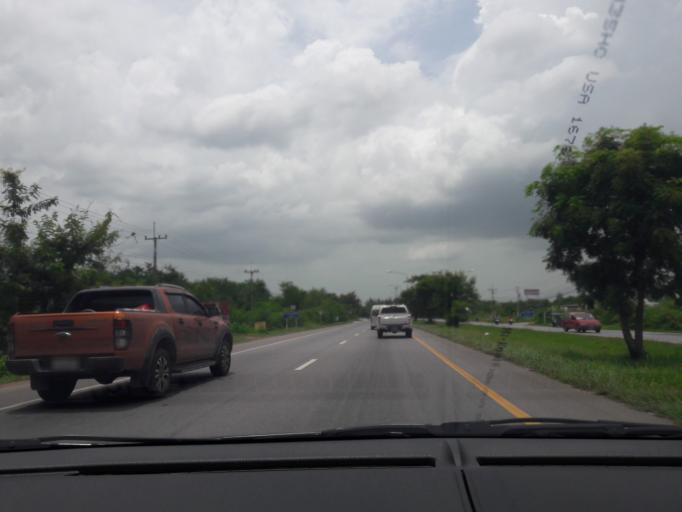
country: TH
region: Nakhon Ratchasima
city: Chaloem Phra Kiat
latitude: 15.0709
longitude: 102.2090
